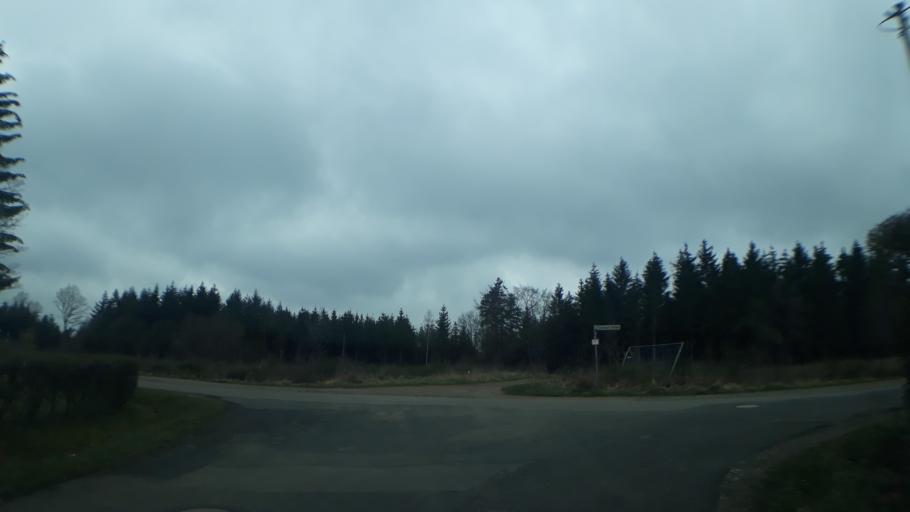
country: DE
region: North Rhine-Westphalia
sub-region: Regierungsbezirk Koln
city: Schleiden
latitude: 50.5244
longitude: 6.5058
